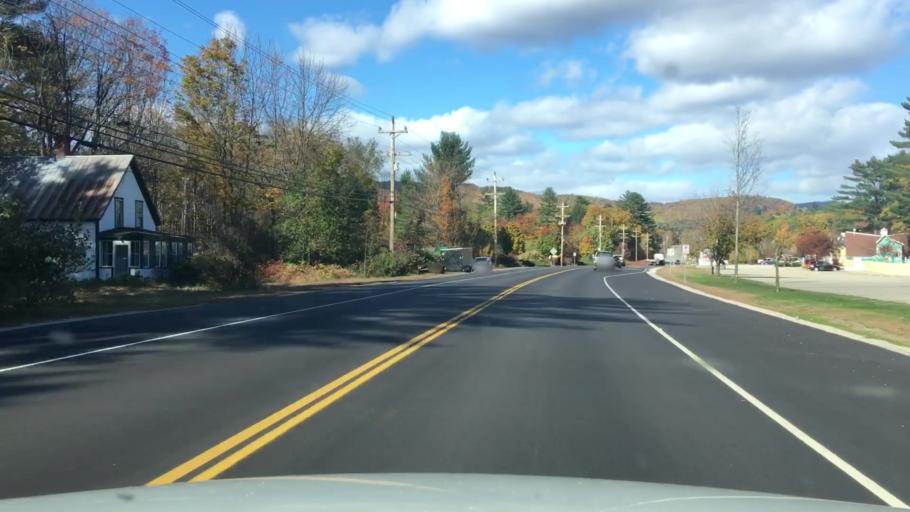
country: US
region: New Hampshire
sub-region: Carroll County
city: North Conway
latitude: 44.1144
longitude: -71.1830
